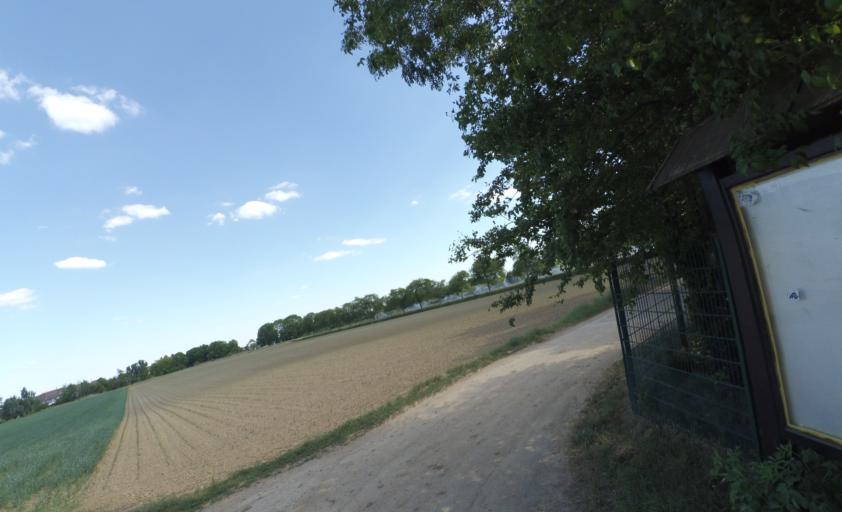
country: DE
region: Rheinland-Pfalz
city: Frankenthal
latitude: 49.5194
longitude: 8.3767
